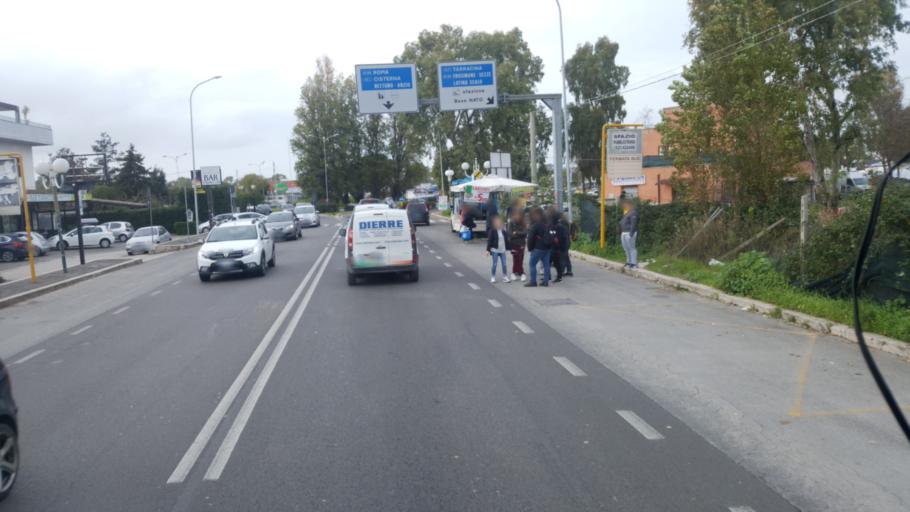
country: IT
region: Latium
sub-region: Provincia di Latina
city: Borgo Podgora
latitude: 41.4814
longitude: 12.8654
